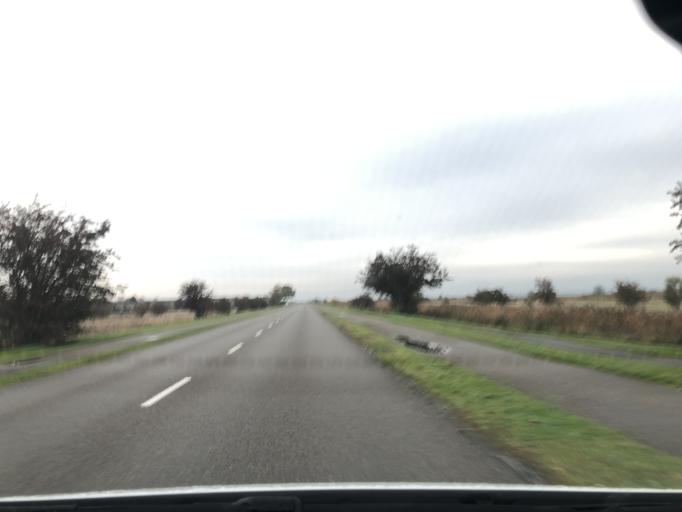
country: DK
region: Capital Region
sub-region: Dragor Kommune
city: Dragor
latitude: 55.5803
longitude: 12.6488
